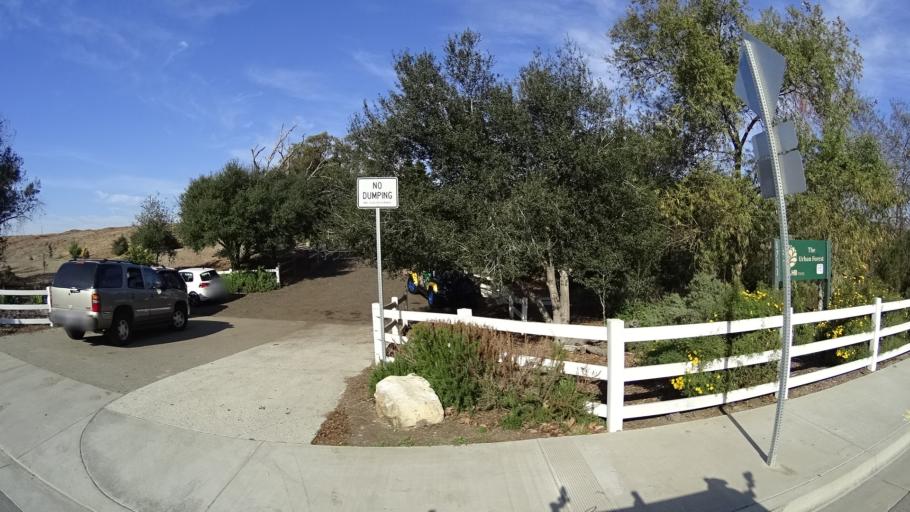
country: US
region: California
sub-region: Orange County
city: Huntington Beach
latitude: 33.6937
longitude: -118.0113
